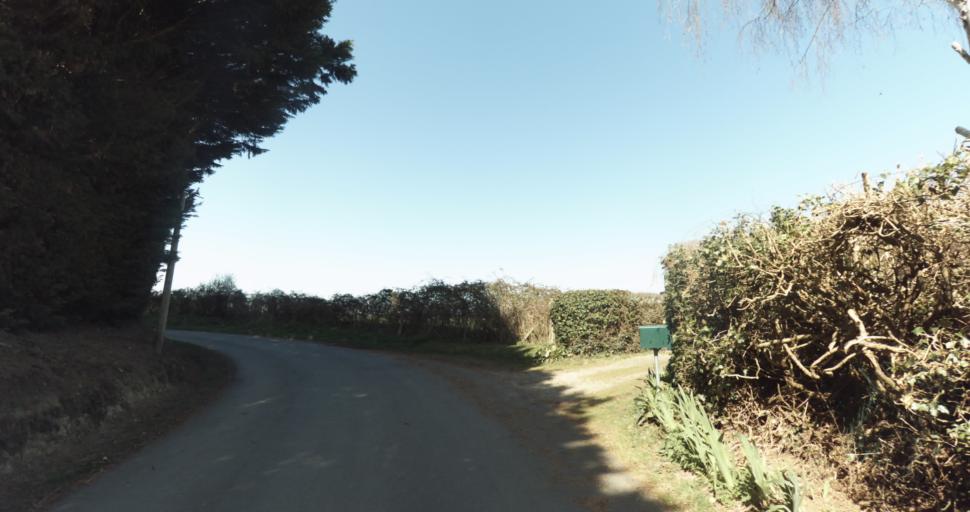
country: FR
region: Lower Normandy
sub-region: Departement du Calvados
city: Saint-Pierre-sur-Dives
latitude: 48.9906
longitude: -0.0212
